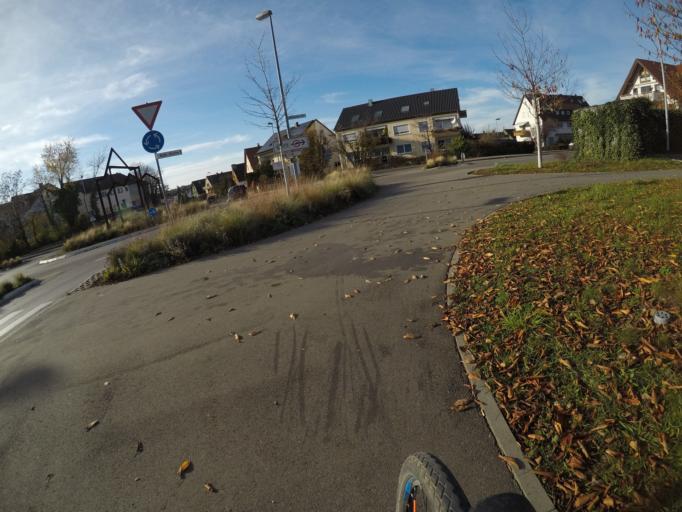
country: DE
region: Baden-Wuerttemberg
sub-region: Regierungsbezirk Stuttgart
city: Waiblingen
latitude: 48.8088
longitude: 9.3259
